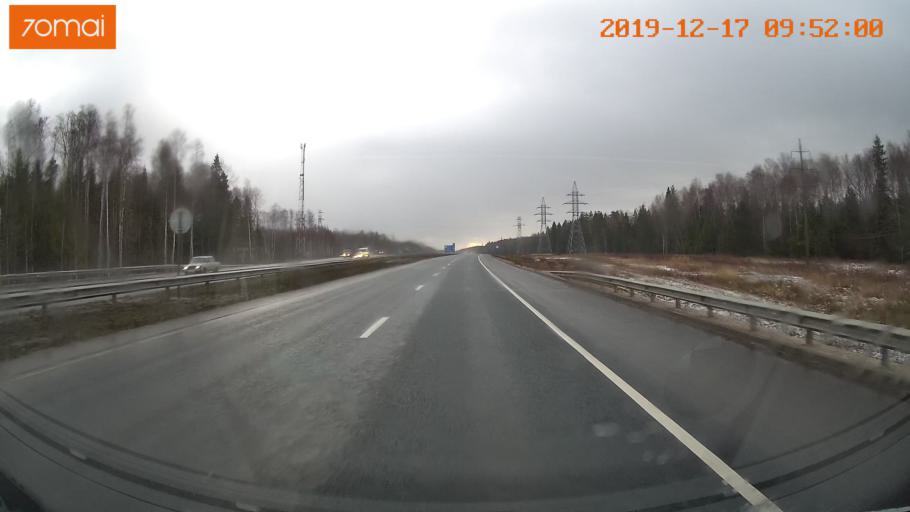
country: RU
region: Vladimir
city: Kommunar
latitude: 56.0375
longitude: 40.5306
